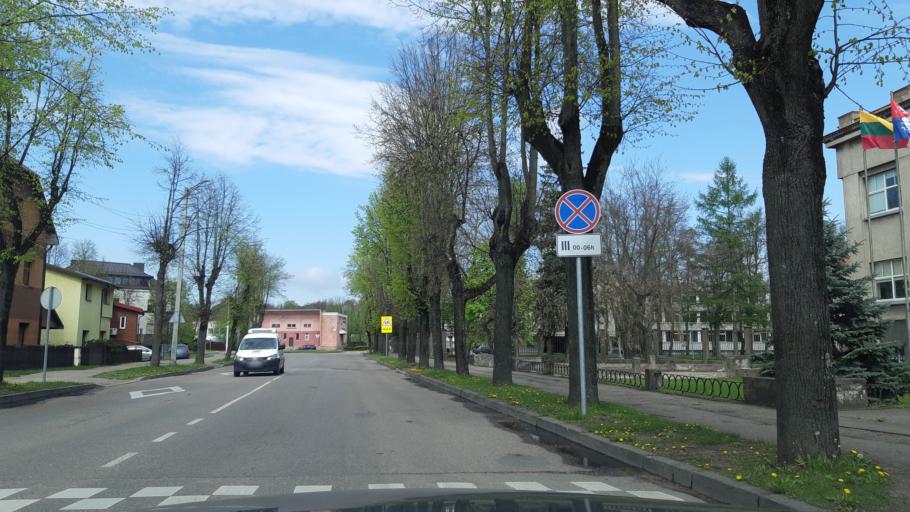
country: LT
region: Kauno apskritis
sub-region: Kaunas
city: Kaunas
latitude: 54.9080
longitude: 23.8795
